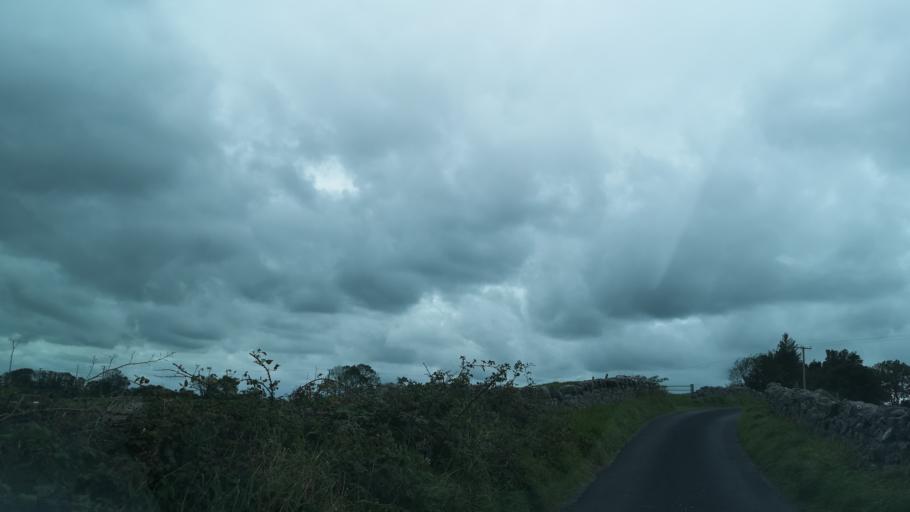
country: IE
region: Connaught
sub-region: County Galway
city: Athenry
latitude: 53.3110
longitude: -8.7437
